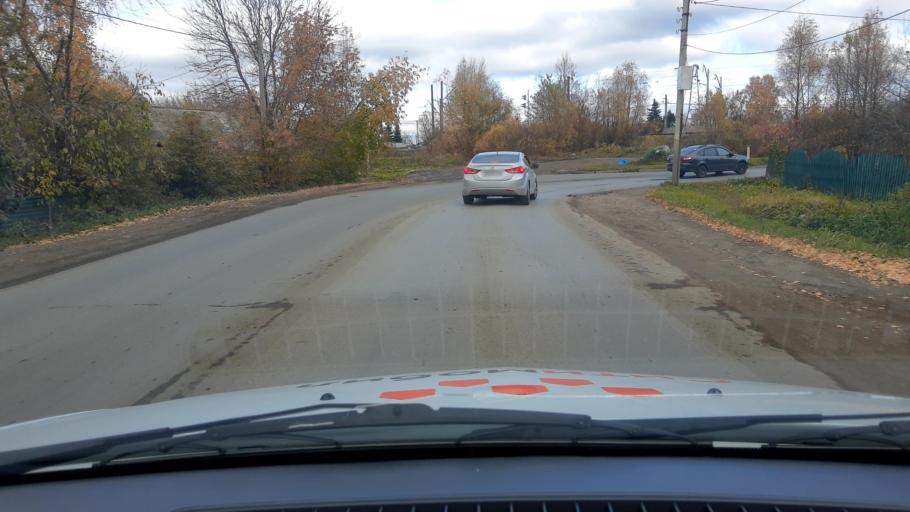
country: RU
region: Bashkortostan
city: Iglino
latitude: 54.7755
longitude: 56.2280
